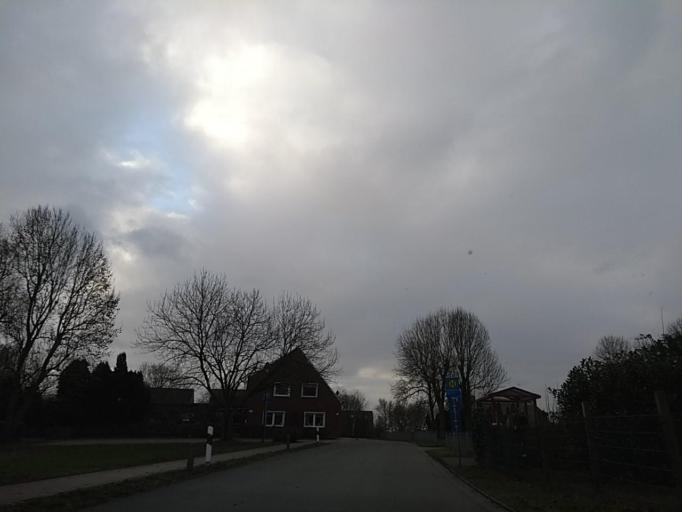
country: DE
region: Lower Saxony
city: Jemgum
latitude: 53.3087
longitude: 7.2937
